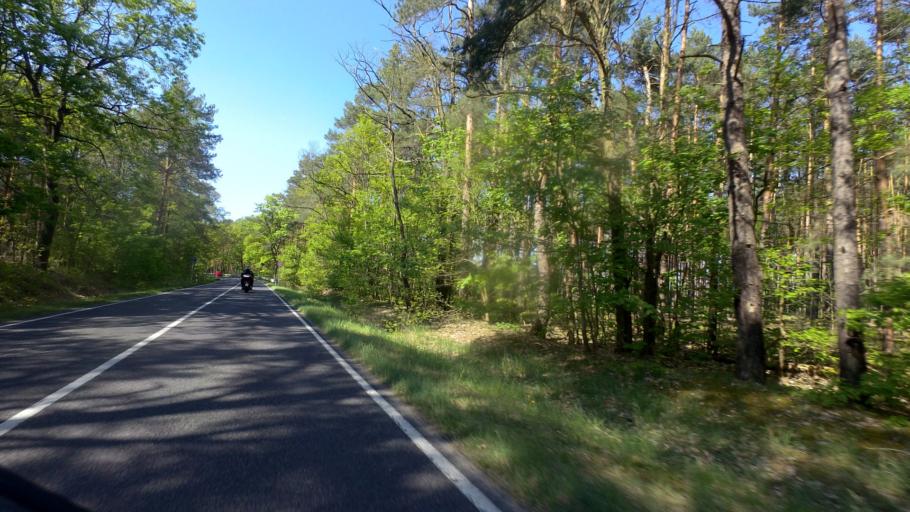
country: DE
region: Brandenburg
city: Bestensee
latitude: 52.2192
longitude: 13.6857
